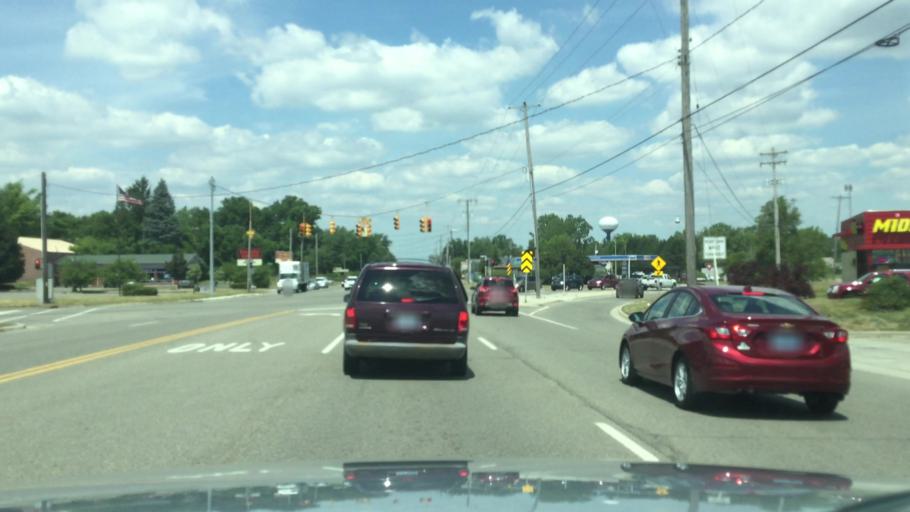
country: US
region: Michigan
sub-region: Genesee County
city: Grand Blanc
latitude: 42.9459
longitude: -83.6521
